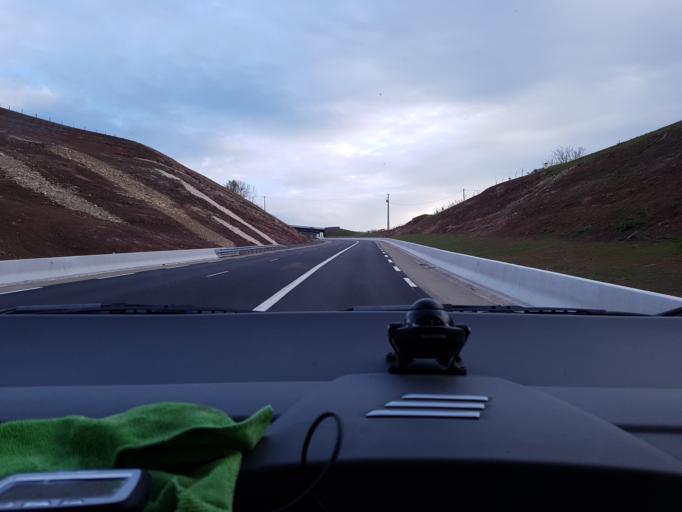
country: FR
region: Midi-Pyrenees
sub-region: Departement de l'Aveyron
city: Espalion
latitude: 44.5150
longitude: 2.7332
